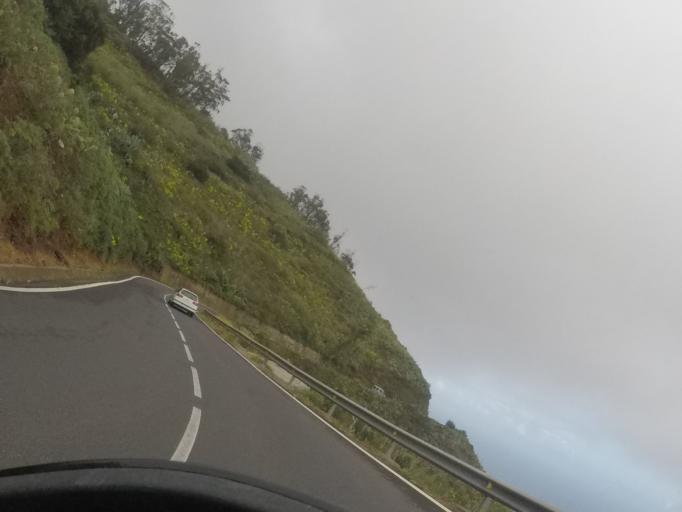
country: ES
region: Canary Islands
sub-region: Provincia de Santa Cruz de Tenerife
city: Tacoronte
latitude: 28.5049
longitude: -16.3796
